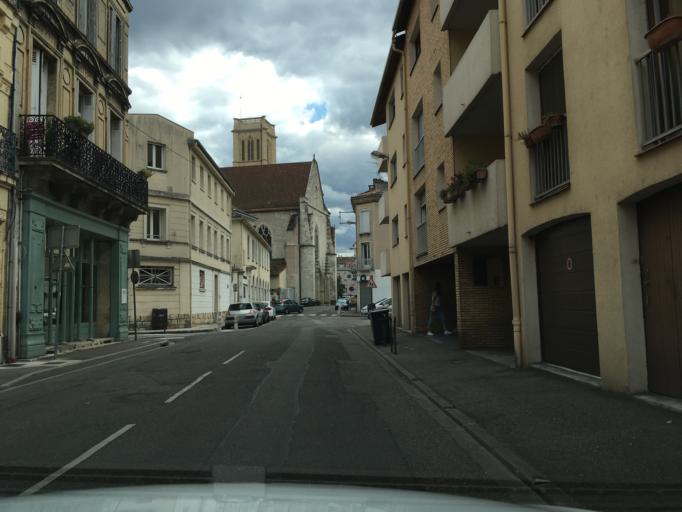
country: FR
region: Aquitaine
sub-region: Departement du Lot-et-Garonne
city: Agen
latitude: 44.2078
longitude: 0.6186
